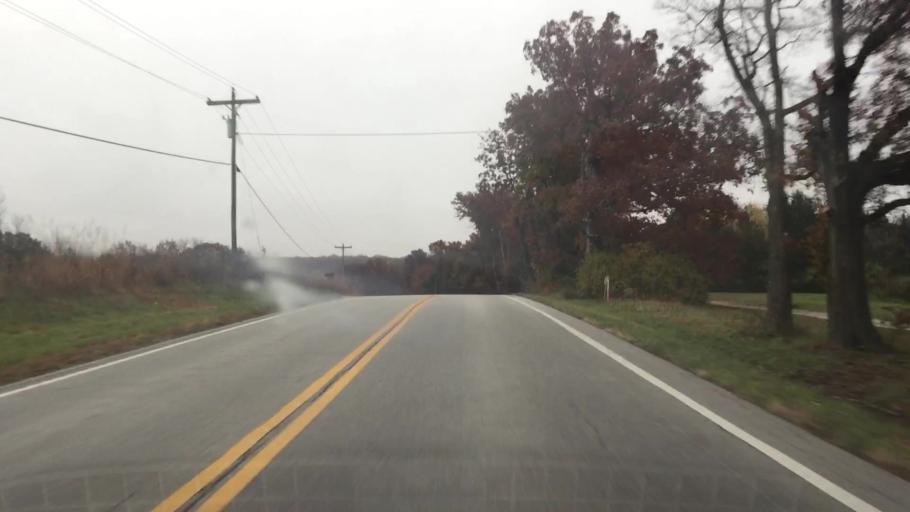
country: US
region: Missouri
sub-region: Callaway County
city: Fulton
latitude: 38.8844
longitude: -92.0944
